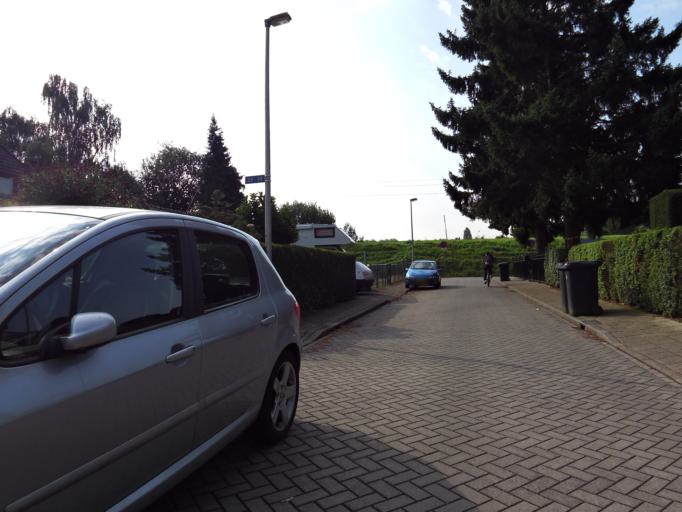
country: NL
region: Limburg
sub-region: Gemeente Heerlen
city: Heerlen
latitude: 50.8913
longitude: 5.9967
